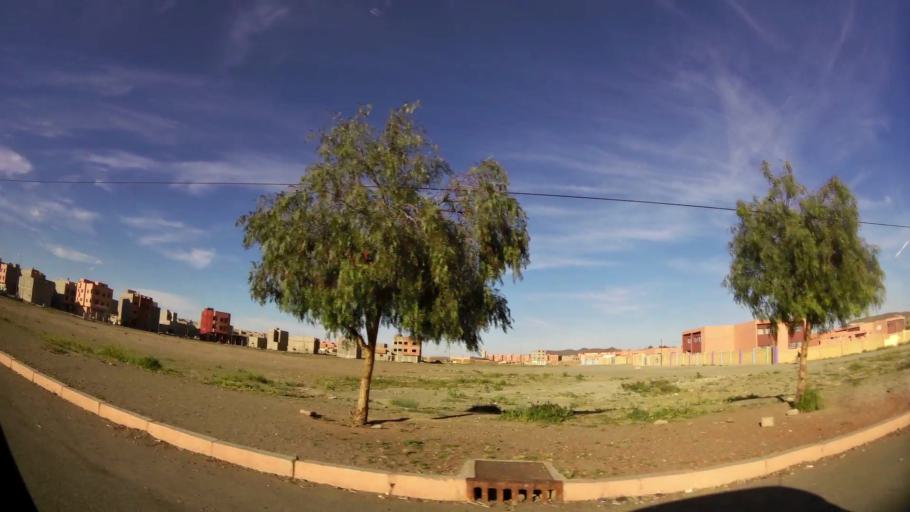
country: MA
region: Marrakech-Tensift-Al Haouz
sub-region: Marrakech
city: Marrakesh
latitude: 31.7616
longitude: -8.0993
